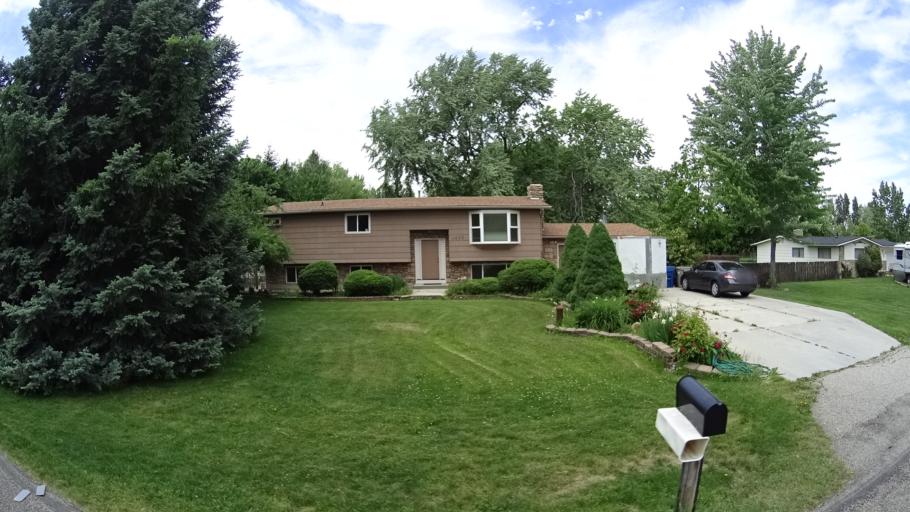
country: US
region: Idaho
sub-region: Ada County
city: Eagle
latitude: 43.6439
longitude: -116.3244
